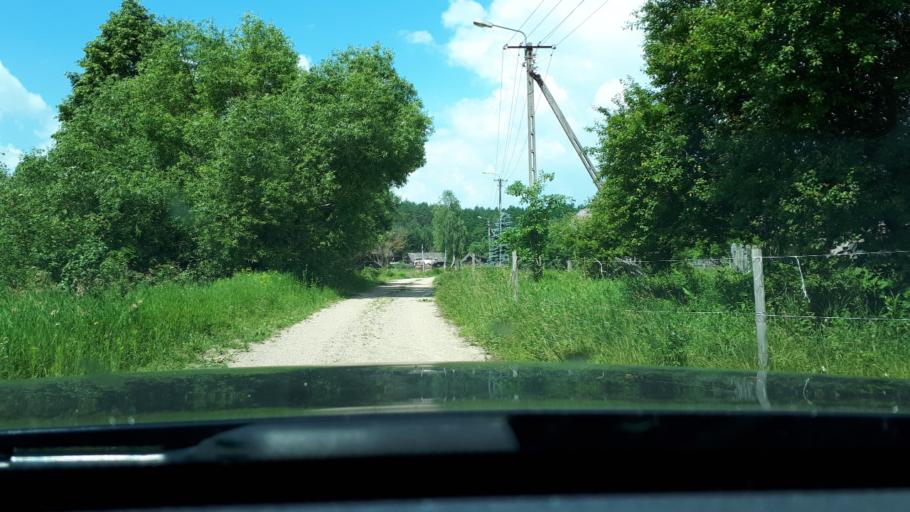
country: PL
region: Podlasie
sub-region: Powiat bialostocki
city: Suprasl
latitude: 53.2435
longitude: 23.3530
